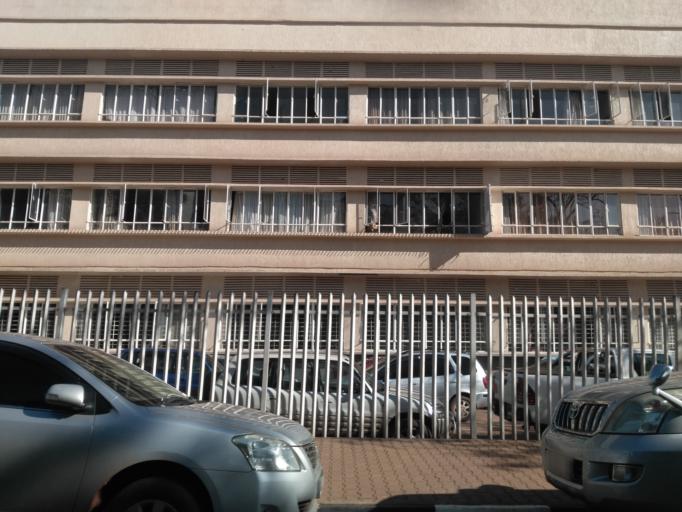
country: UG
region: Central Region
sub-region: Kampala District
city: Kampala
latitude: 0.3150
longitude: 32.5882
